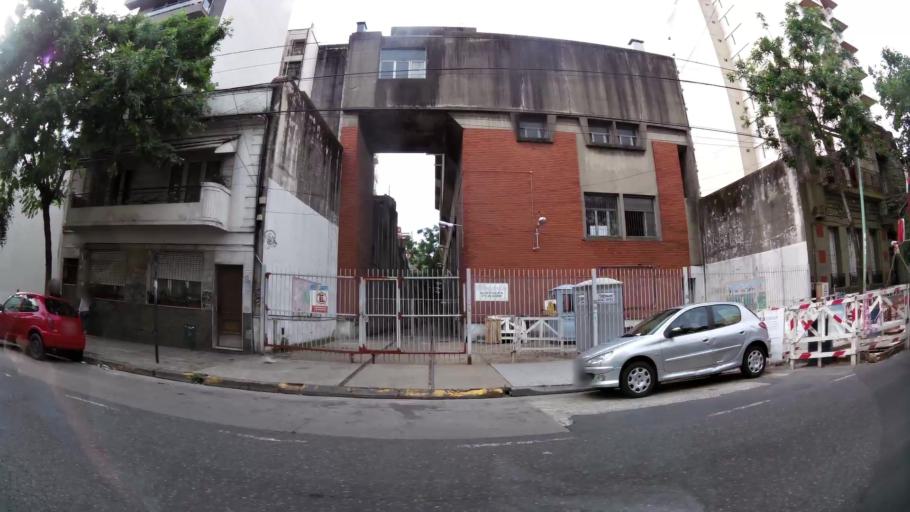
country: AR
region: Buenos Aires F.D.
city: Villa Santa Rita
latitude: -34.6323
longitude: -58.4653
